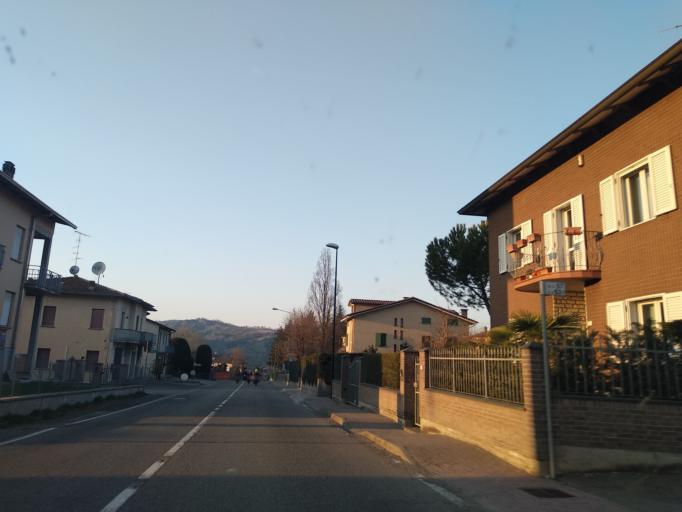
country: IT
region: Emilia-Romagna
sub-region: Provincia di Reggio Emilia
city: Vezzano sul Crostolo
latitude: 44.5644
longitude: 10.5289
